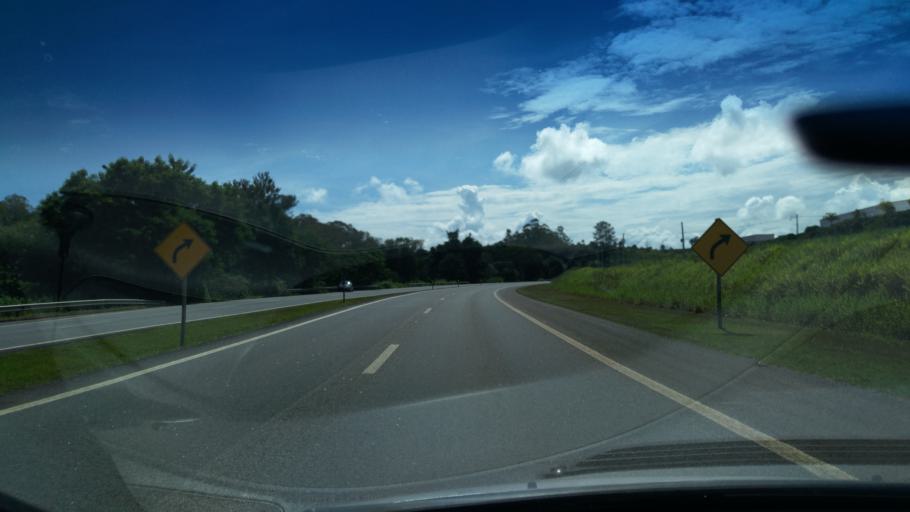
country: BR
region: Sao Paulo
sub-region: Santo Antonio Do Jardim
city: Espirito Santo do Pinhal
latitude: -22.2251
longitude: -46.7935
